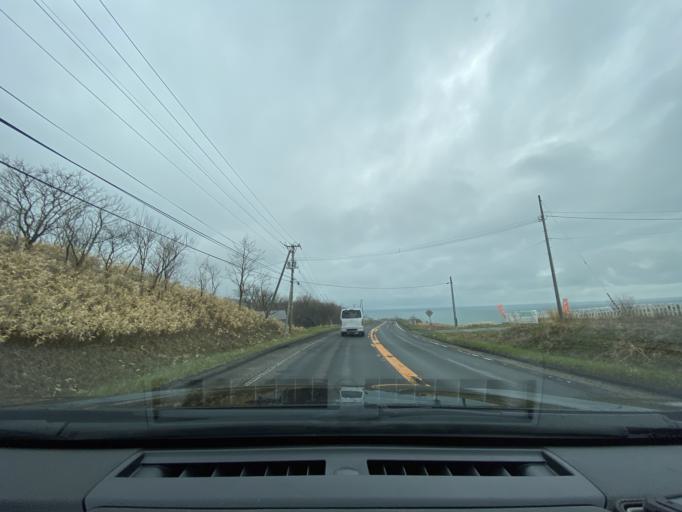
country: JP
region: Hokkaido
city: Ishikari
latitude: 43.3845
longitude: 141.4324
